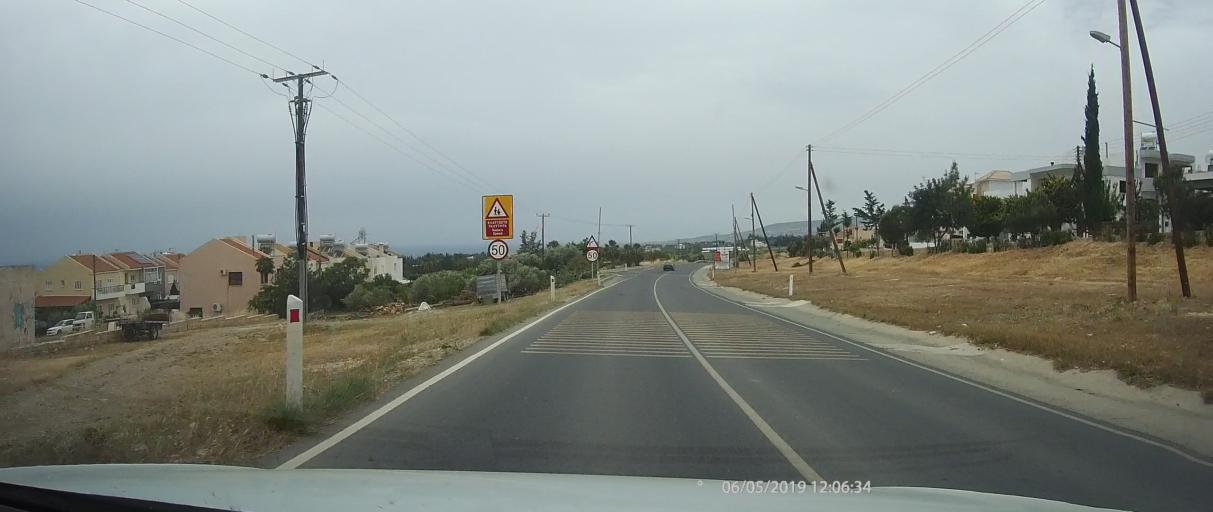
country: CY
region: Pafos
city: Empa
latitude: 34.8184
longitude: 32.4245
